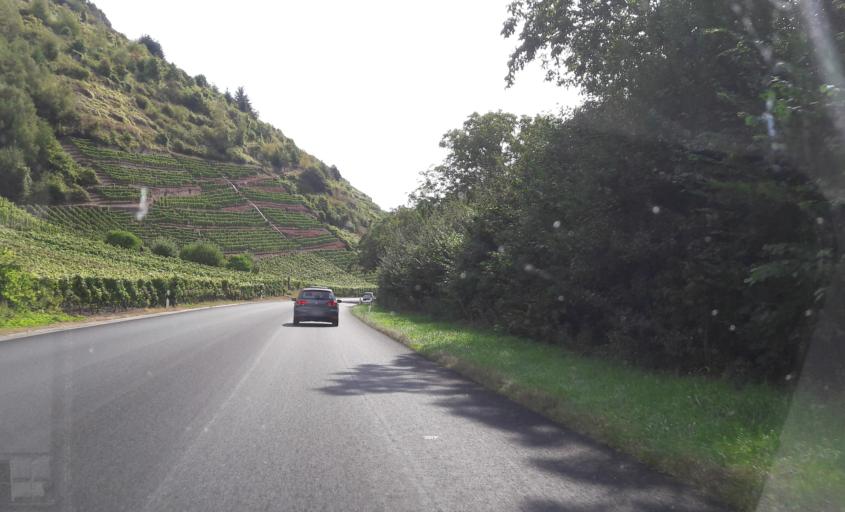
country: DE
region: Rheinland-Pfalz
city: Ediger-Eller
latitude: 50.0907
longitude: 7.1674
